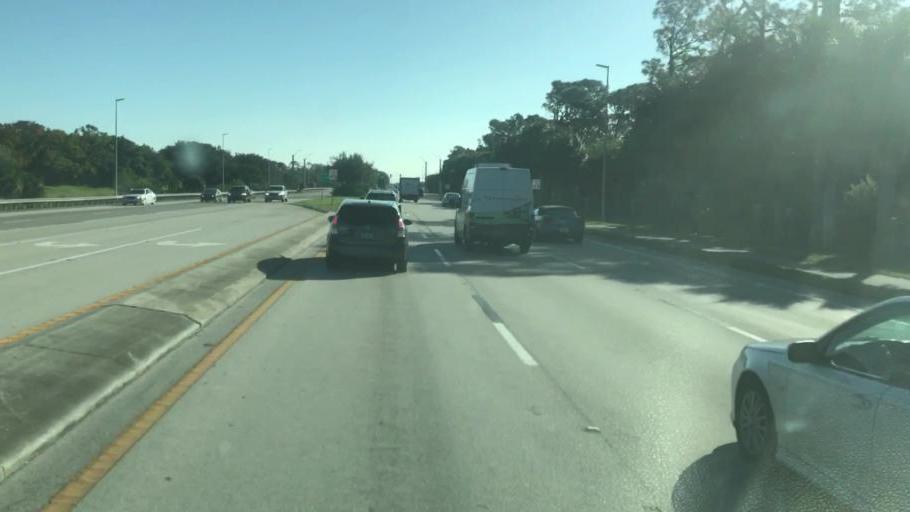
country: US
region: Florida
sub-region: Lee County
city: Villas
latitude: 26.5464
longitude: -81.8670
